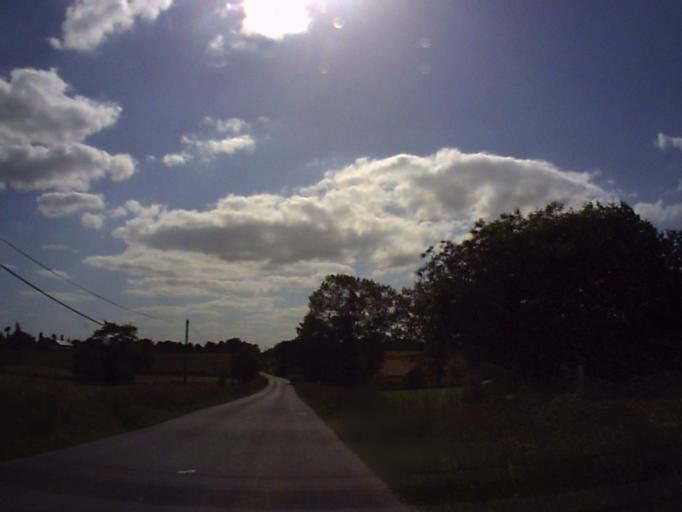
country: FR
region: Brittany
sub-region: Departement d'Ille-et-Vilaine
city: Bedee
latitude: 48.1779
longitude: -1.9637
